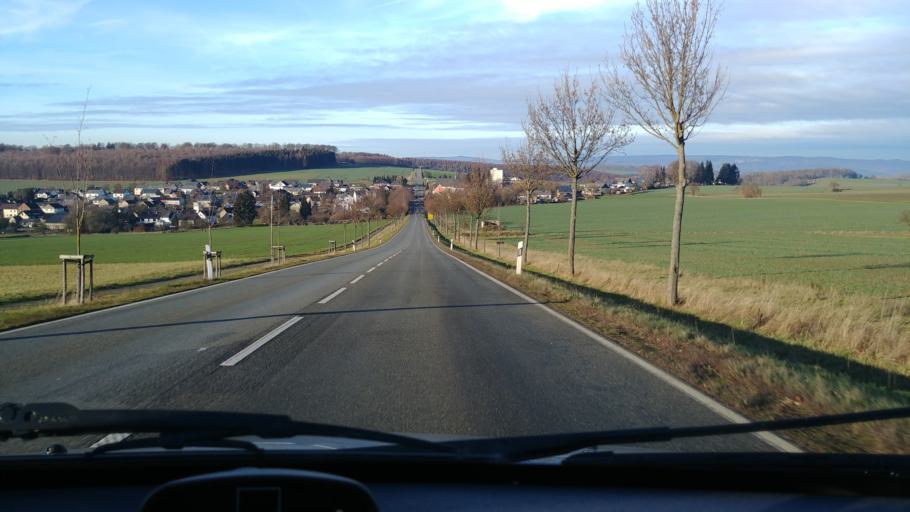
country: DE
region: Rheinland-Pfalz
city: Pohl
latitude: 50.2456
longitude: 7.8722
